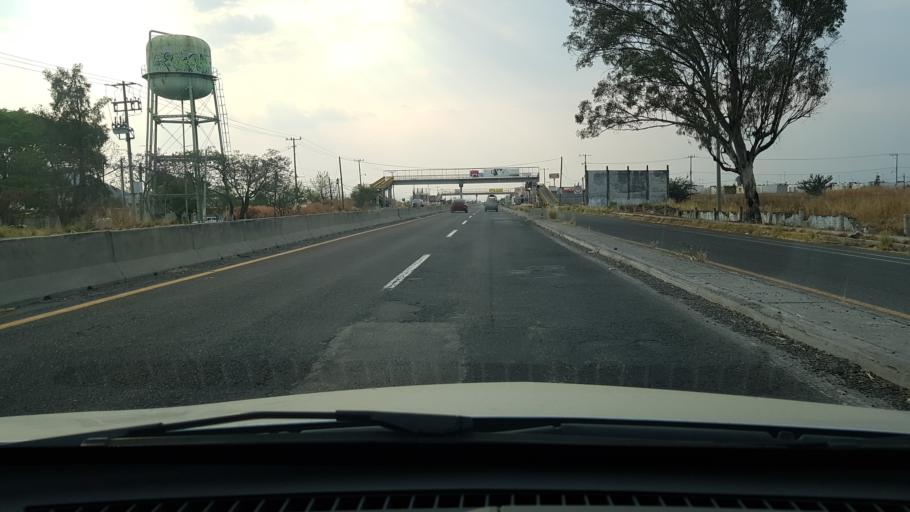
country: MX
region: Morelos
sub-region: Ayala
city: Unidad Habitacional Mariano Matamoros
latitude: 18.7501
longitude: -98.8501
